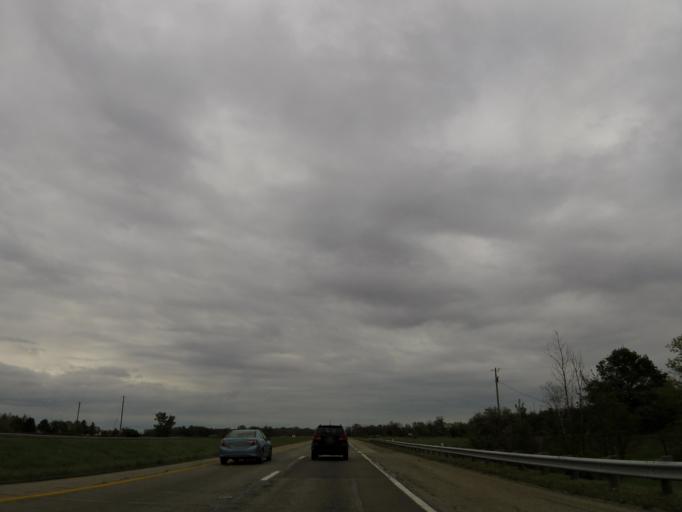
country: US
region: Ohio
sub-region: Madison County
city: Bethel
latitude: 39.7430
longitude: -83.3352
